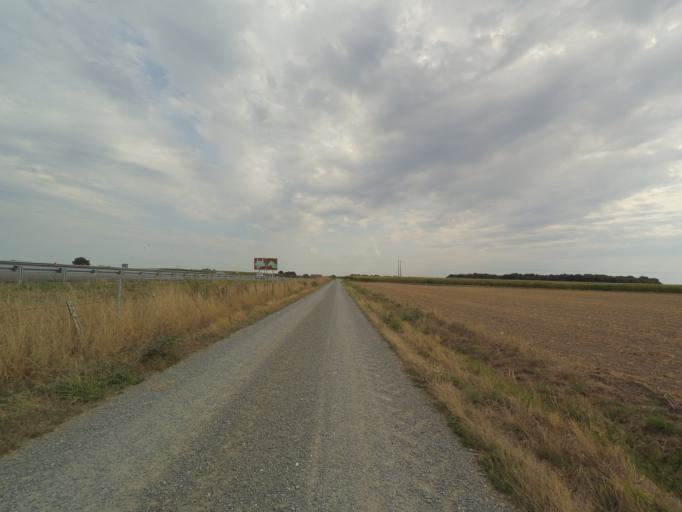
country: FR
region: Pays de la Loire
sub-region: Departement de la Vendee
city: Bouffere
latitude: 46.9782
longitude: -1.3733
